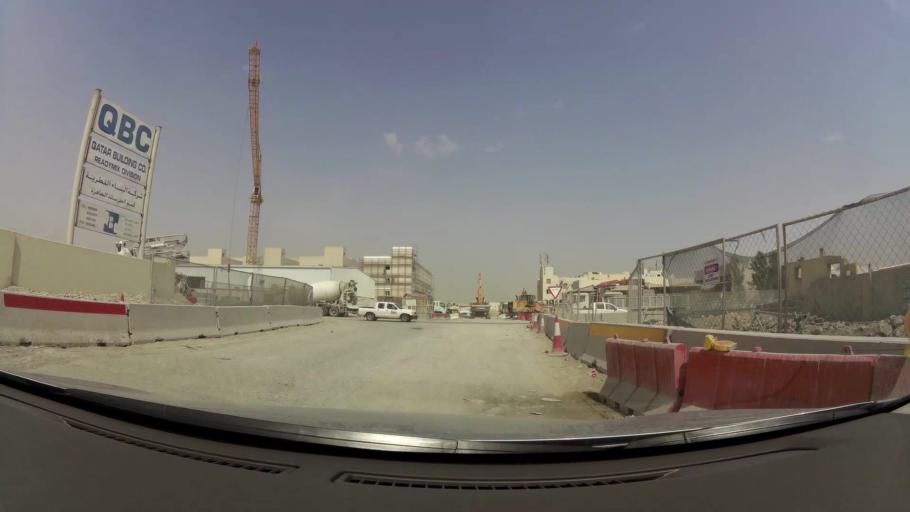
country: QA
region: Al Wakrah
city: Al Wukayr
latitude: 25.1711
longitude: 51.4383
